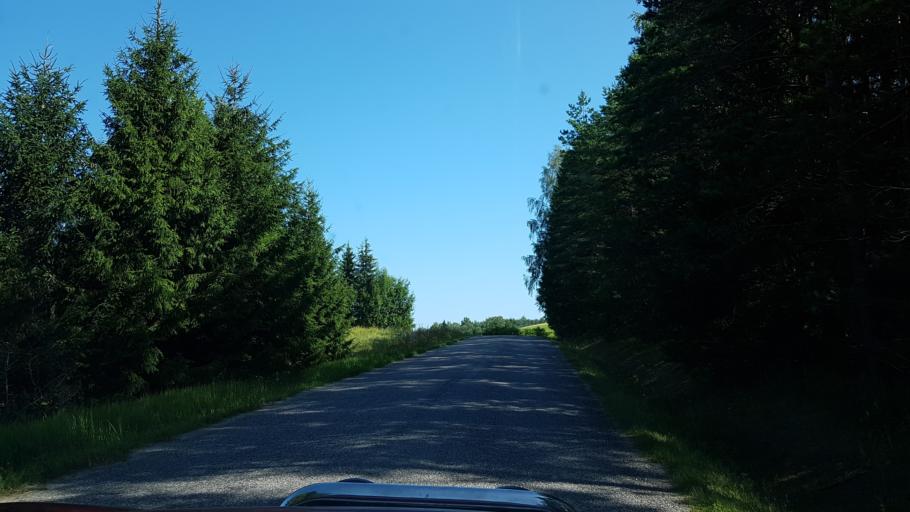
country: EE
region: Vorumaa
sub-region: Voru linn
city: Voru
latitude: 57.7199
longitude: 27.1004
